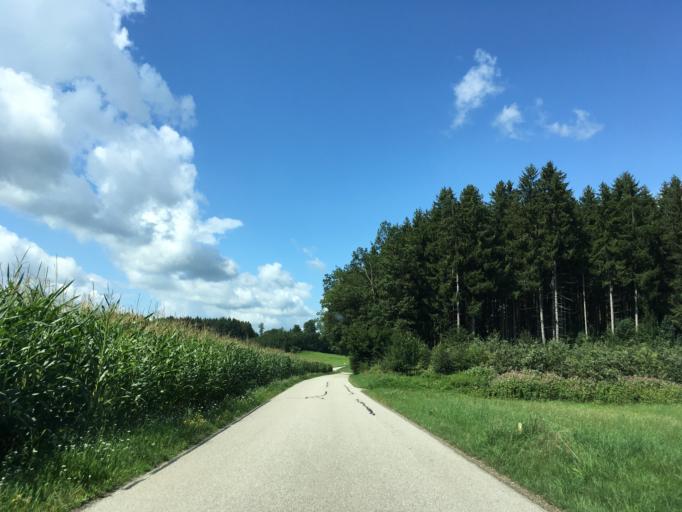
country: DE
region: Bavaria
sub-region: Upper Bavaria
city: Pittenhart
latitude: 47.9732
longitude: 12.3669
